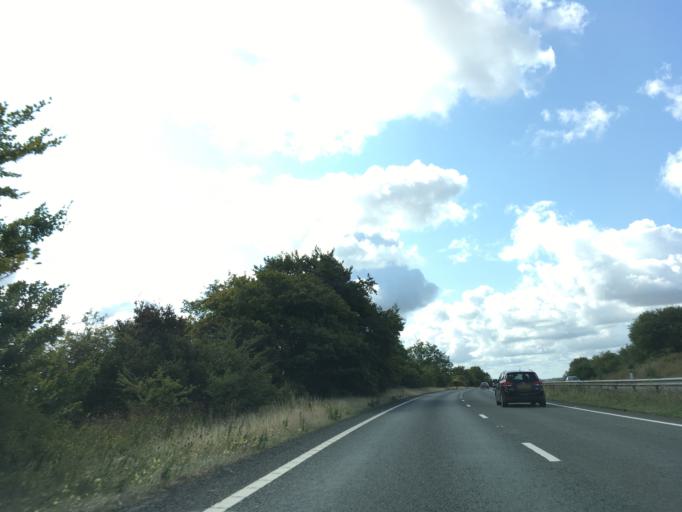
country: GB
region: England
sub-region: Hampshire
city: Highclere
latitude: 51.3121
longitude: -1.3334
